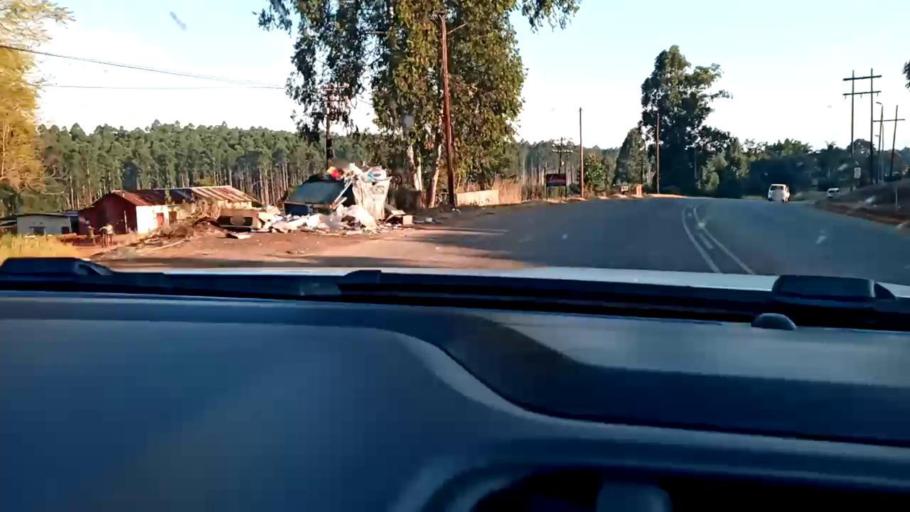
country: ZA
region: Limpopo
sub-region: Mopani District Municipality
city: Duiwelskloof
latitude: -23.7003
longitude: 30.1357
